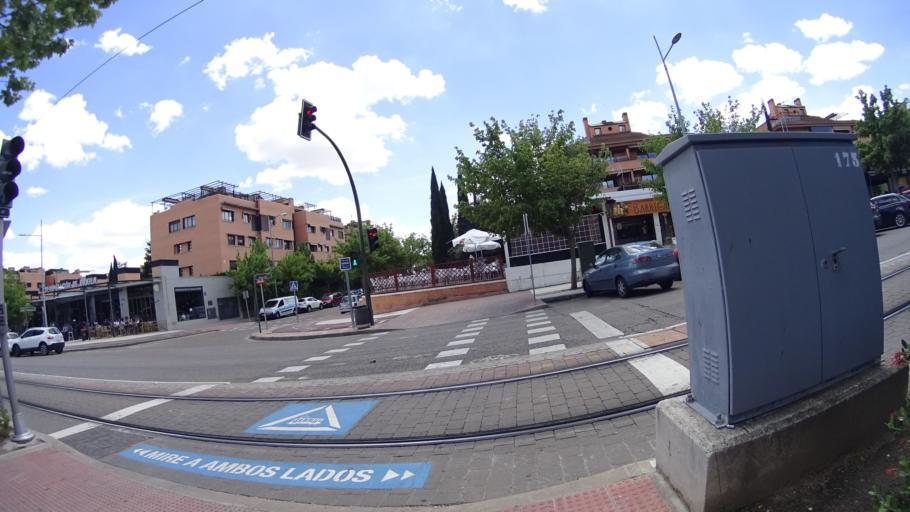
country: ES
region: Madrid
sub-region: Provincia de Madrid
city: Boadilla del Monte
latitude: 40.4051
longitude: -3.8946
